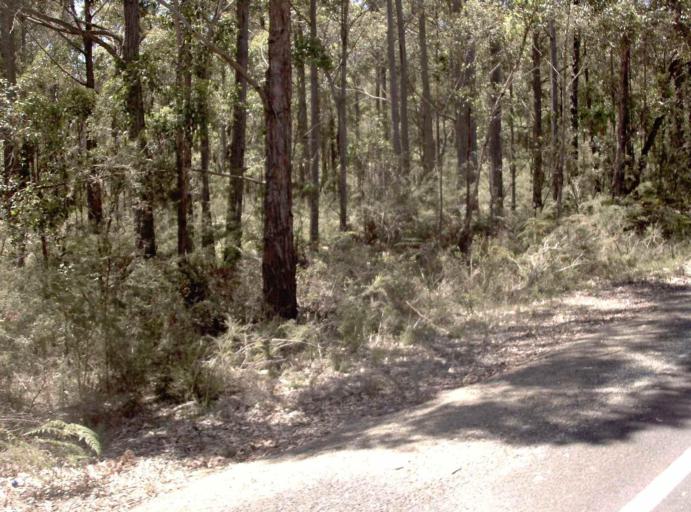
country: AU
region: Victoria
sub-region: East Gippsland
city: Lakes Entrance
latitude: -37.7302
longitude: 148.1209
